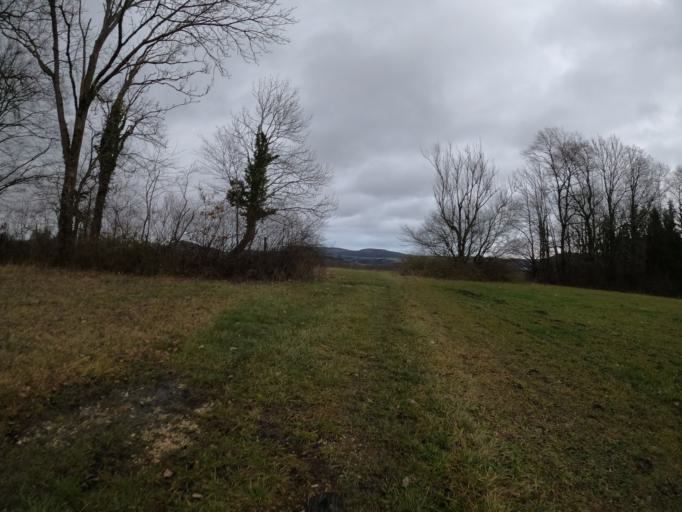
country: DE
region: Baden-Wuerttemberg
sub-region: Regierungsbezirk Stuttgart
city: Sussen
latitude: 48.7029
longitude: 9.7759
